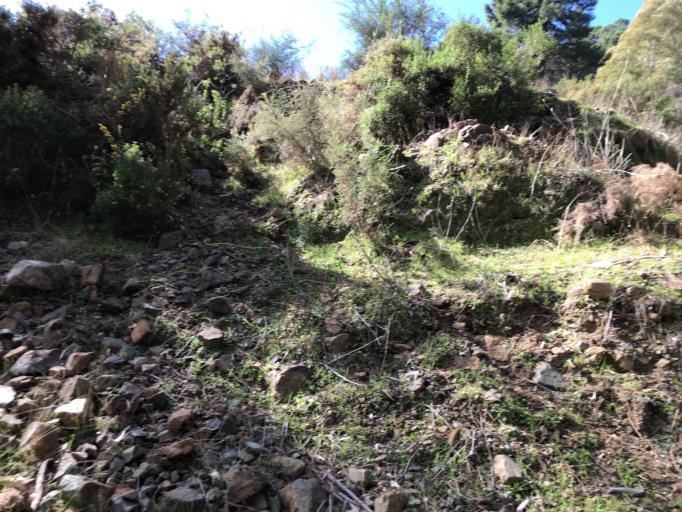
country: ES
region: Andalusia
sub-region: Provincia de Malaga
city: Tolox
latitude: 36.6752
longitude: -4.9154
